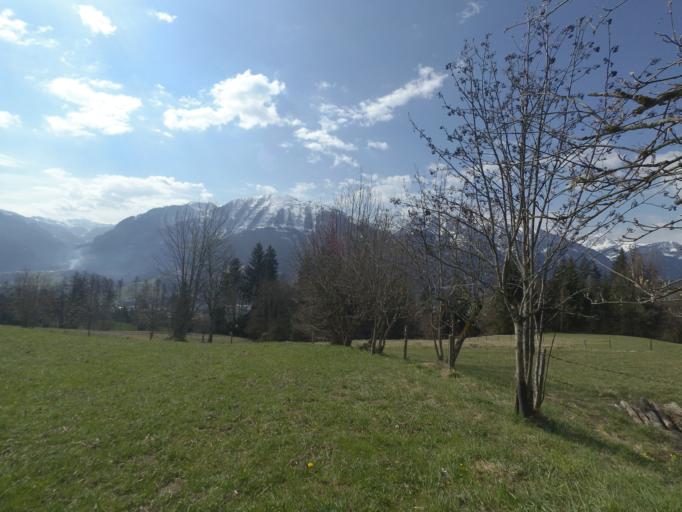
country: AT
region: Salzburg
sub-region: Politischer Bezirk Sankt Johann im Pongau
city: Sankt Veit im Pongau
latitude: 47.3376
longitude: 13.1418
